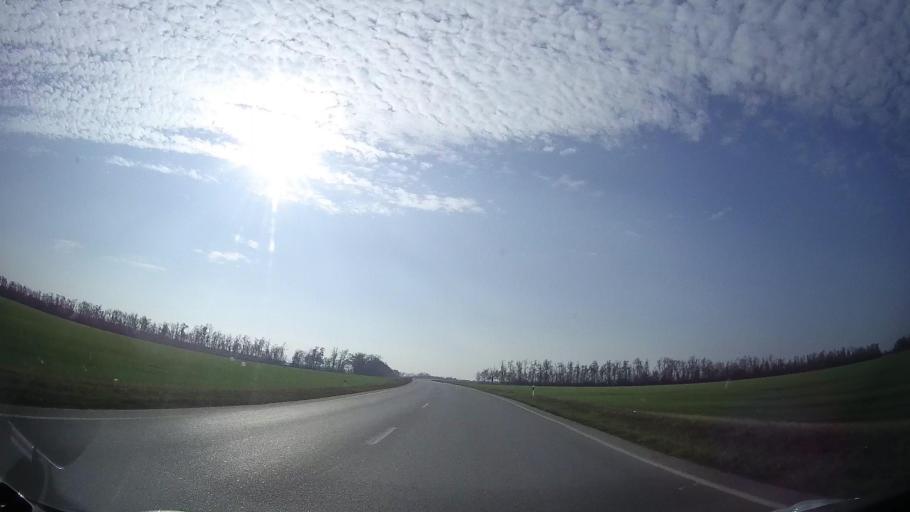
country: RU
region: Rostov
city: Tselina
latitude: 46.5205
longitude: 41.0732
